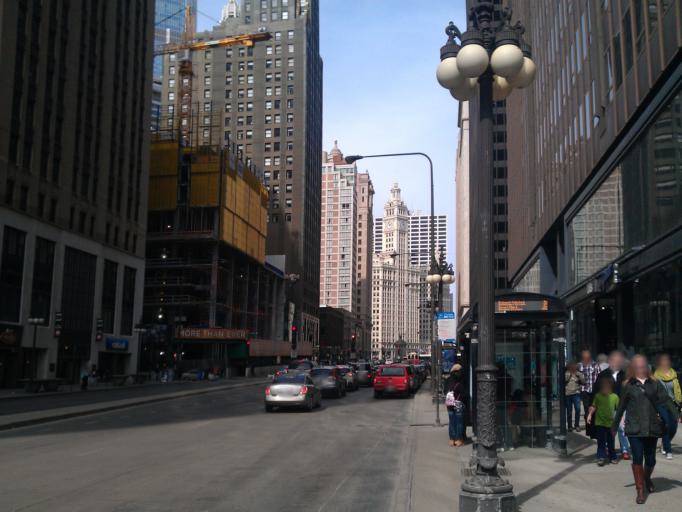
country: US
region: Illinois
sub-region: Cook County
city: Chicago
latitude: 41.8849
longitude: -87.6243
